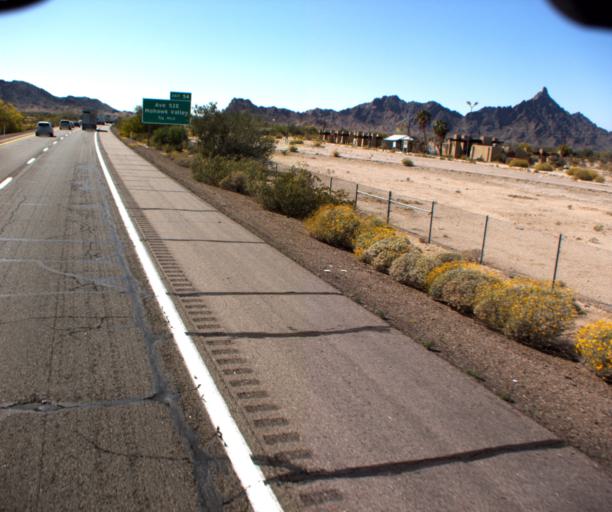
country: US
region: Arizona
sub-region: Yuma County
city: Wellton
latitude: 32.7315
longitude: -113.7141
